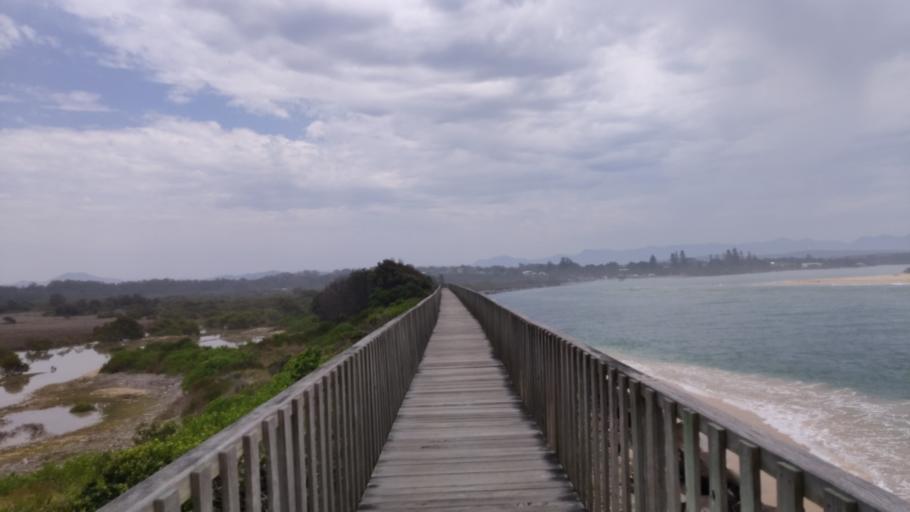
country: AU
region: New South Wales
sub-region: Coffs Harbour
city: Bonville
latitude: -30.5026
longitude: 153.0311
